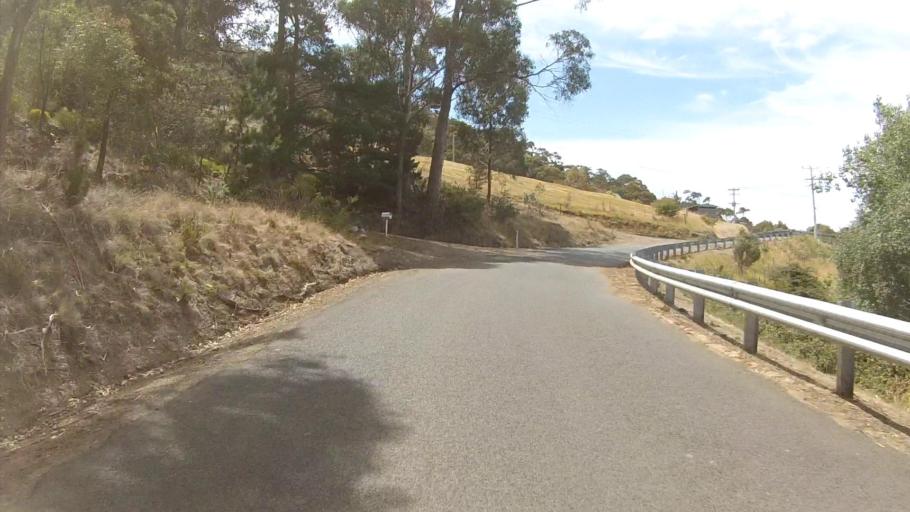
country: AU
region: Tasmania
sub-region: Kingborough
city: Blackmans Bay
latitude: -43.0555
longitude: 147.3350
